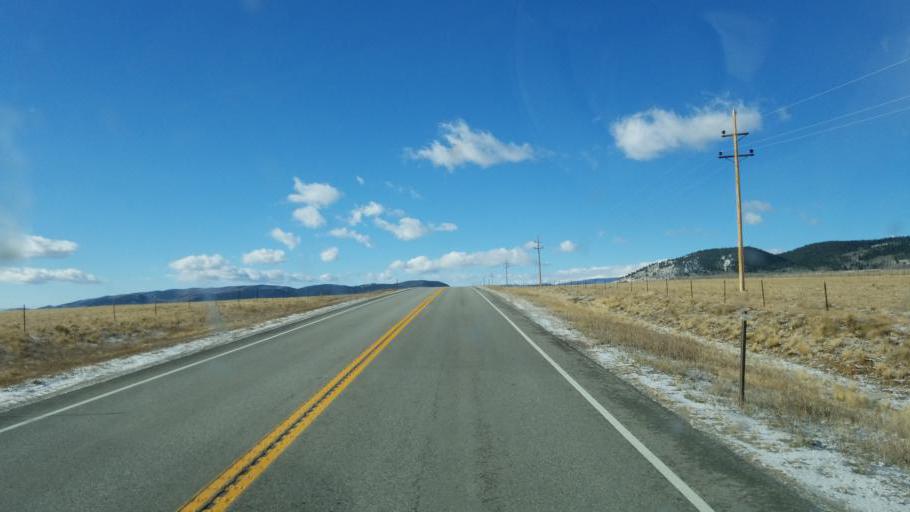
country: US
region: Colorado
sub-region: Park County
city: Fairplay
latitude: 39.3286
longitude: -105.8707
